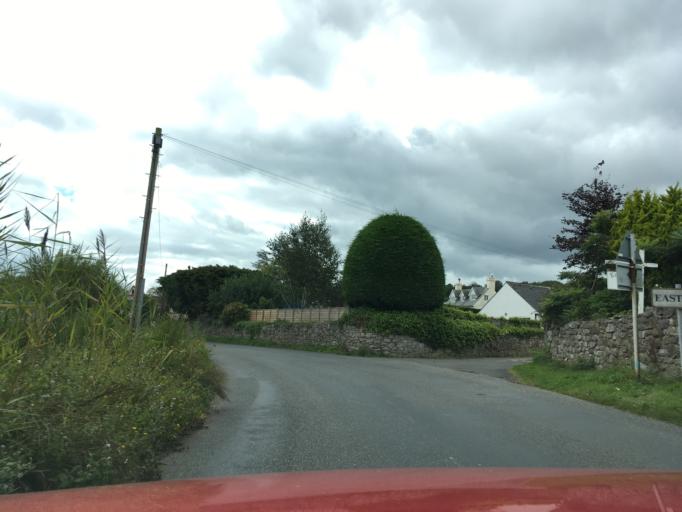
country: GB
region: England
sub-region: Devon
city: Starcross
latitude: 50.6102
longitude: -3.4462
